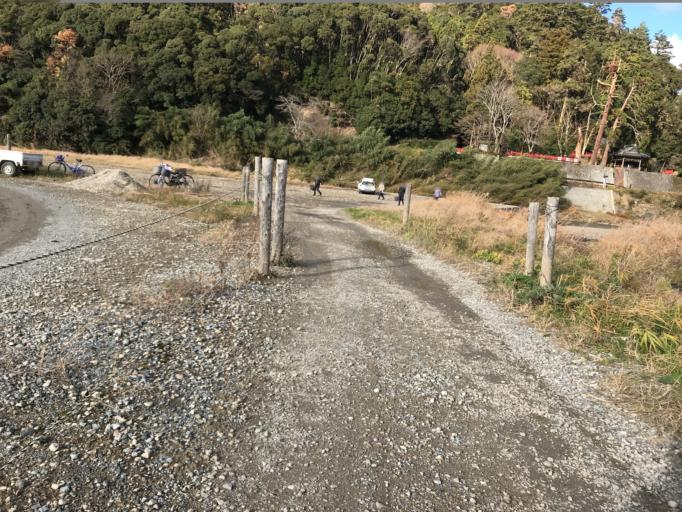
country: JP
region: Kyoto
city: Kameoka
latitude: 35.0144
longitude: 135.6070
